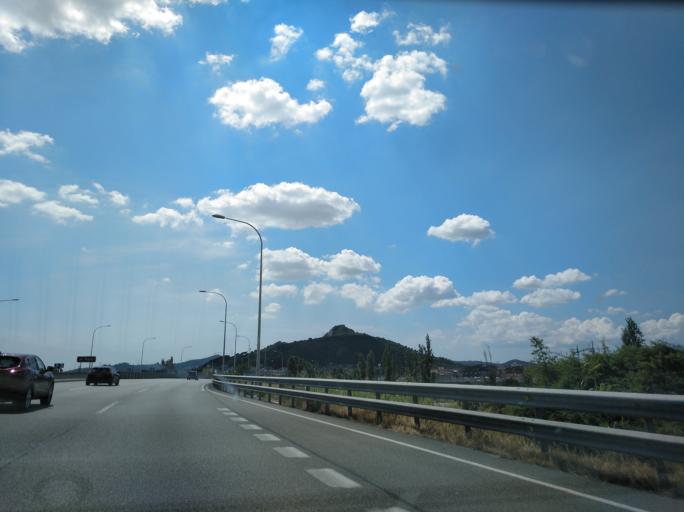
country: ES
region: Catalonia
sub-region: Provincia de Barcelona
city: Montcada i Reixac
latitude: 41.4926
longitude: 2.1900
